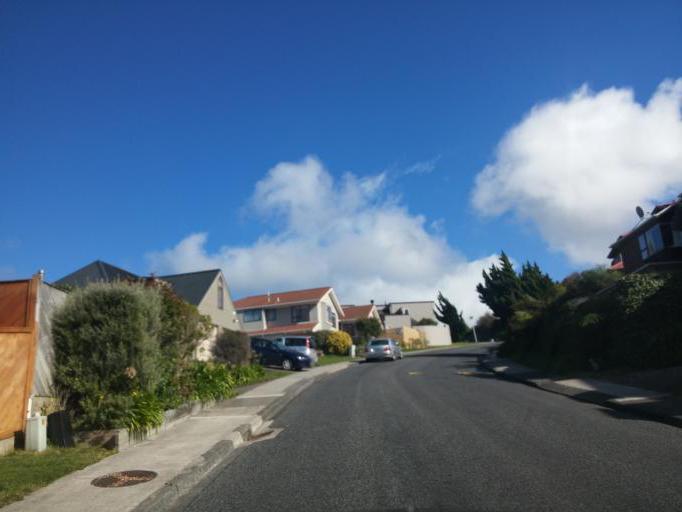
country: NZ
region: Wellington
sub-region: Wellington City
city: Kelburn
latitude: -41.2432
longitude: 174.7792
